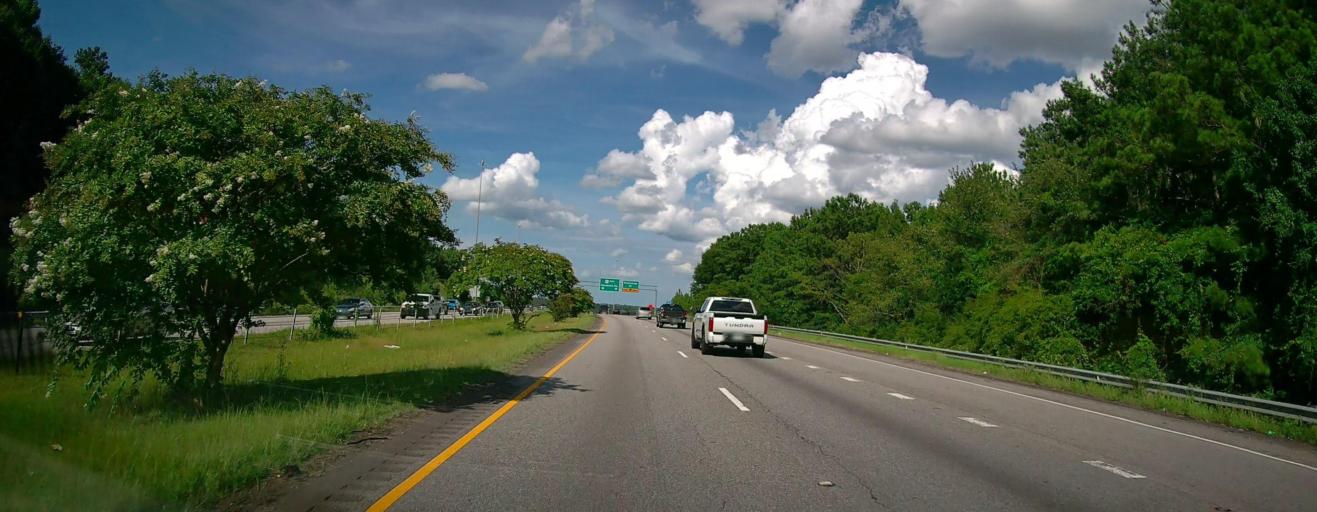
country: US
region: Alabama
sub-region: Russell County
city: Phenix City
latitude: 32.5006
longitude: -85.0125
